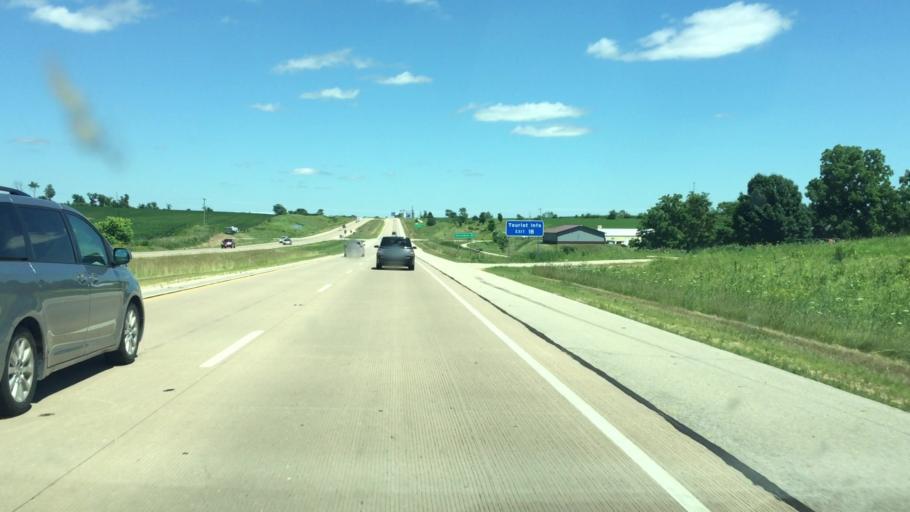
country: US
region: Wisconsin
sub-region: Grant County
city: Platteville
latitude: 42.7109
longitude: -90.5090
